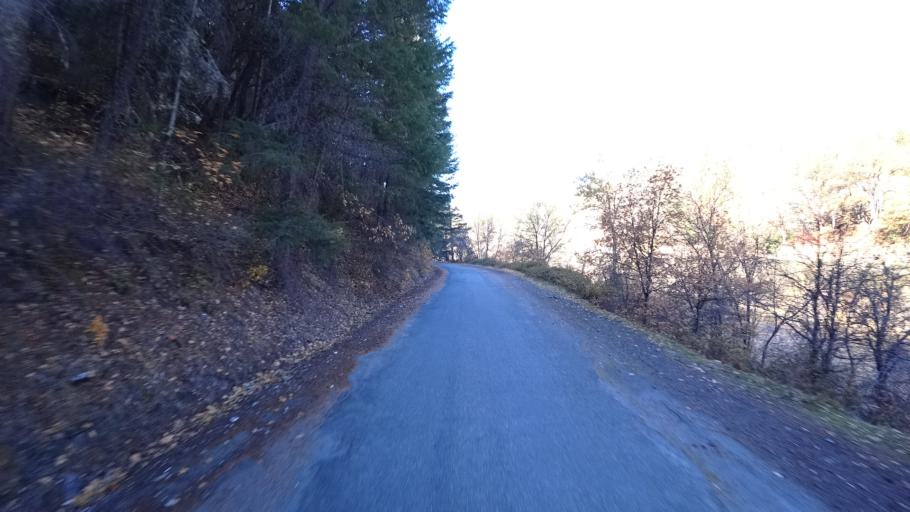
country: US
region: California
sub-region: Siskiyou County
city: Yreka
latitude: 41.8406
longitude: -122.9190
